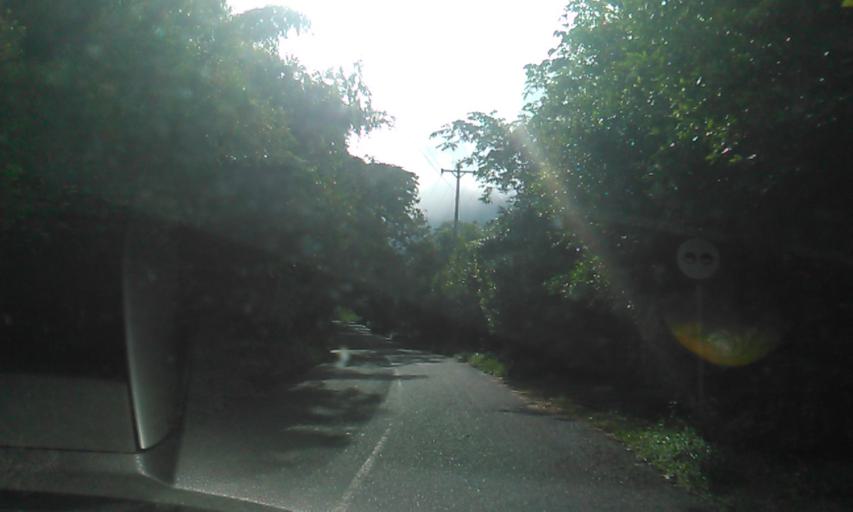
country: CO
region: Quindio
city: Cordoba
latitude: 4.4029
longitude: -75.7242
